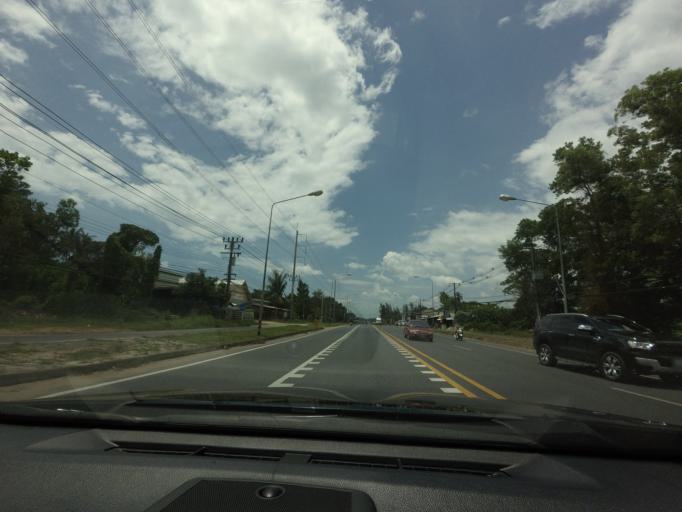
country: TH
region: Phangnga
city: Ban Khao Lak
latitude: 8.6573
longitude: 98.2534
